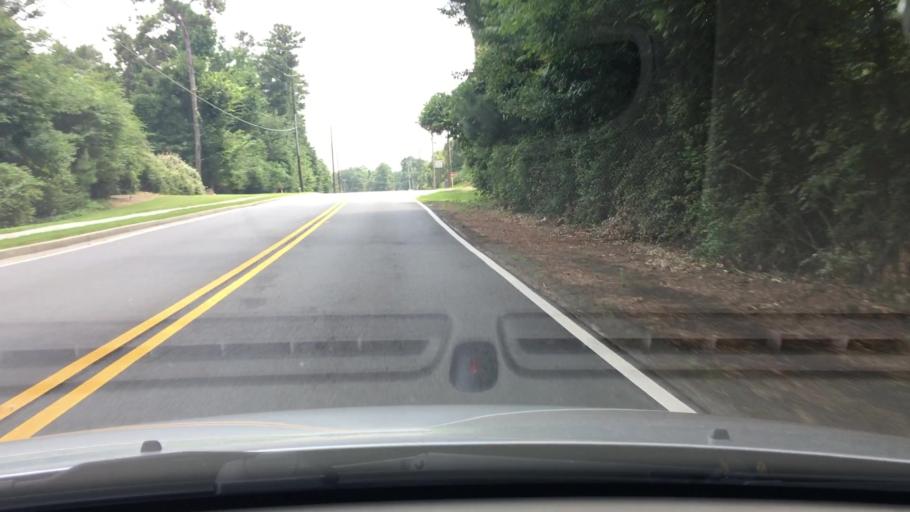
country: US
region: Georgia
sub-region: Fulton County
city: Alpharetta
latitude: 34.0578
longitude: -84.2753
